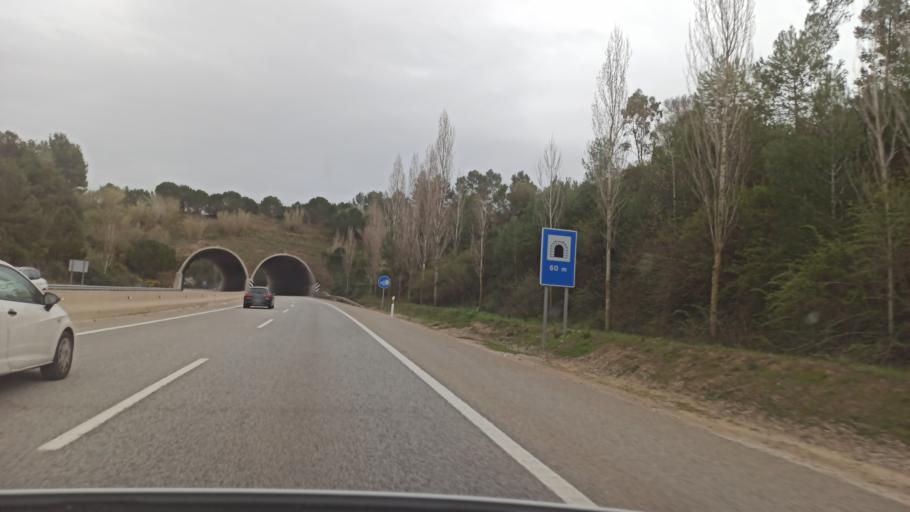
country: ES
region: Catalonia
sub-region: Provincia de Barcelona
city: Cervello
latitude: 41.3910
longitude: 1.9594
